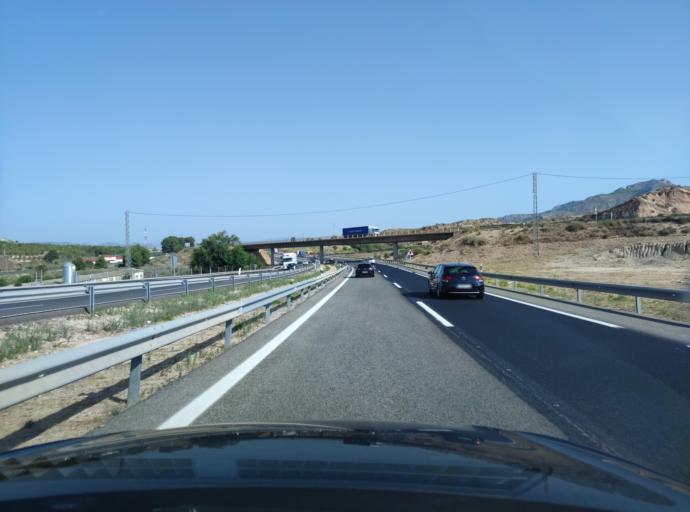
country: ES
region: Valencia
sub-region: Provincia de Alicante
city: Sax
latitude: 38.5519
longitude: -0.8196
